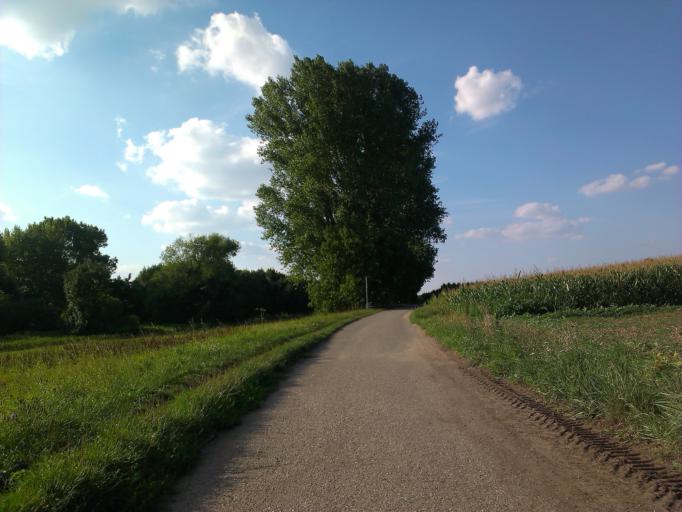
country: DE
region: Baden-Wuerttemberg
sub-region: Karlsruhe Region
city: Edingen-Neckarhausen
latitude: 49.4510
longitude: 8.6141
